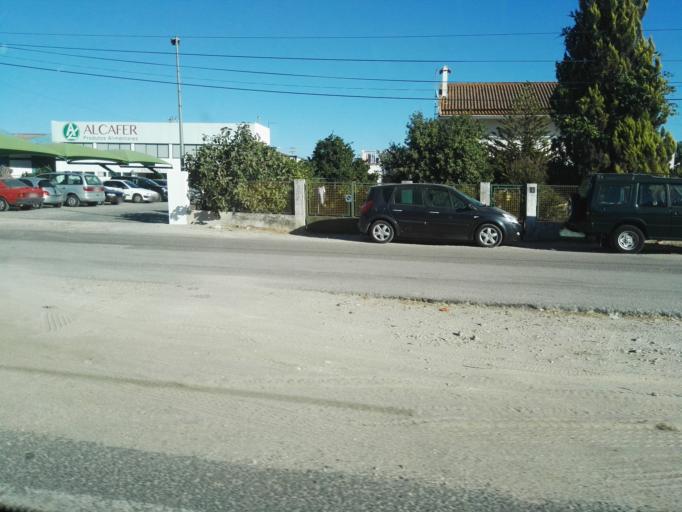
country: PT
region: Santarem
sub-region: Benavente
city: Benavente
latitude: 38.9547
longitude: -8.8246
